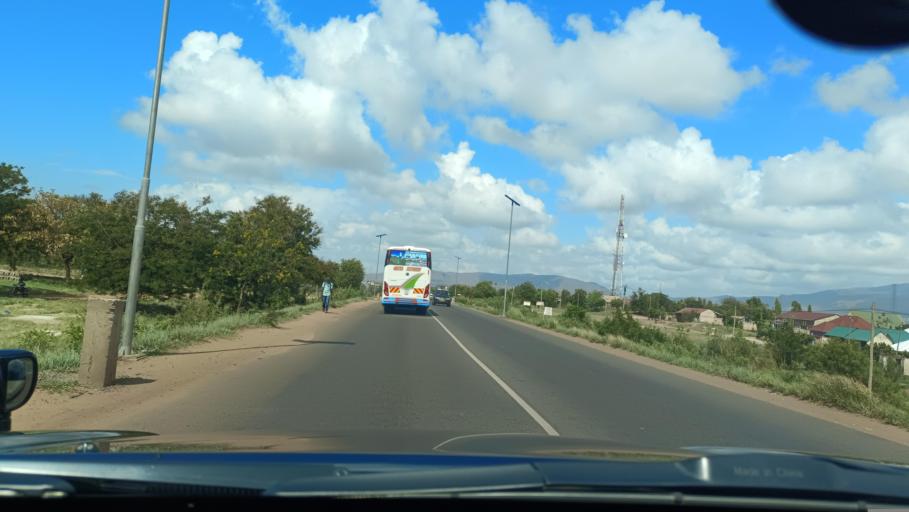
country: TZ
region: Morogoro
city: Morogoro
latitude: -6.8031
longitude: 37.6893
